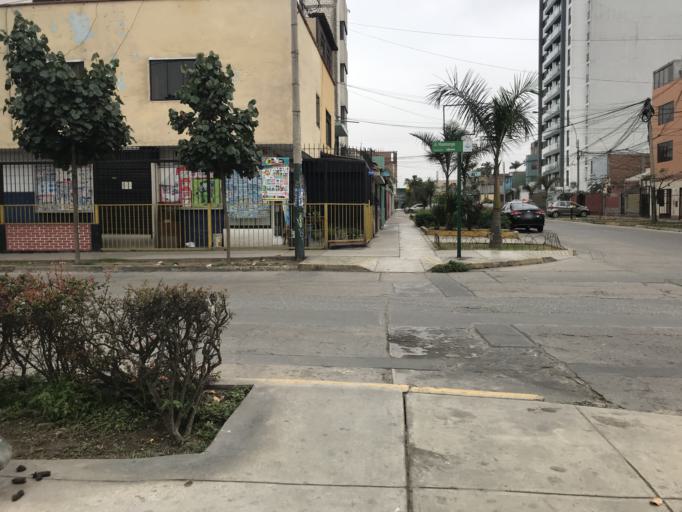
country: PE
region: Lima
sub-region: Lima
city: San Isidro
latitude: -12.0857
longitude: -77.0696
